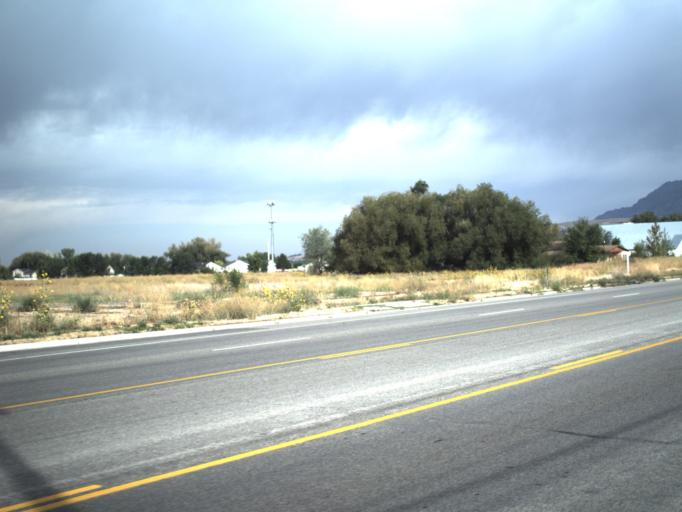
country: US
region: Utah
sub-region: Weber County
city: North Ogden
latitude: 41.2897
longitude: -111.9689
